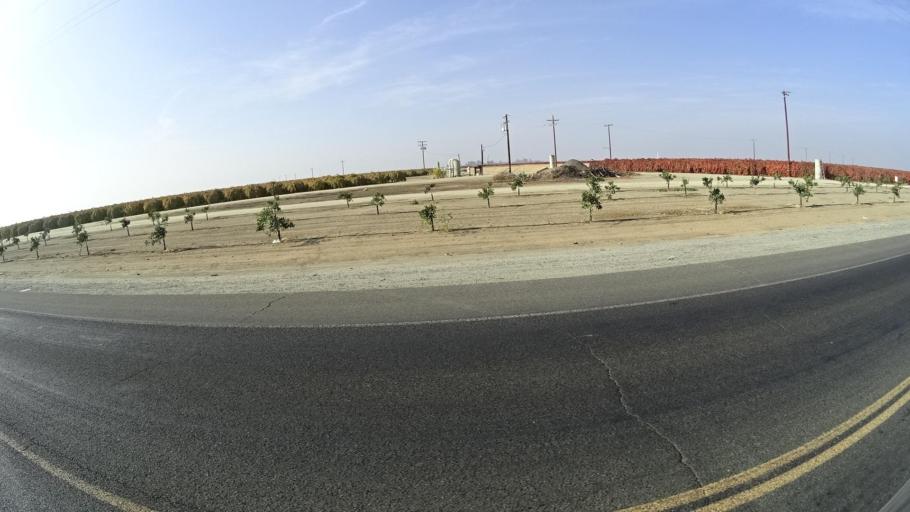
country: US
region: California
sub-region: Tulare County
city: Richgrove
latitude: 35.7320
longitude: -119.1511
